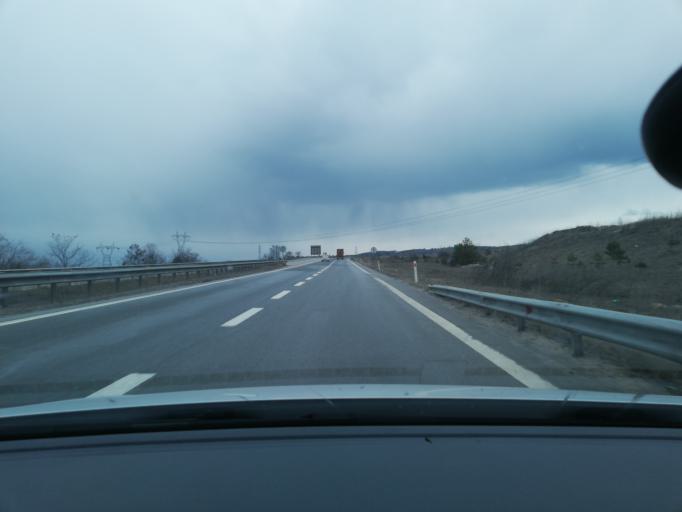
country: TR
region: Bolu
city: Gerede
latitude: 40.7763
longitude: 32.2155
